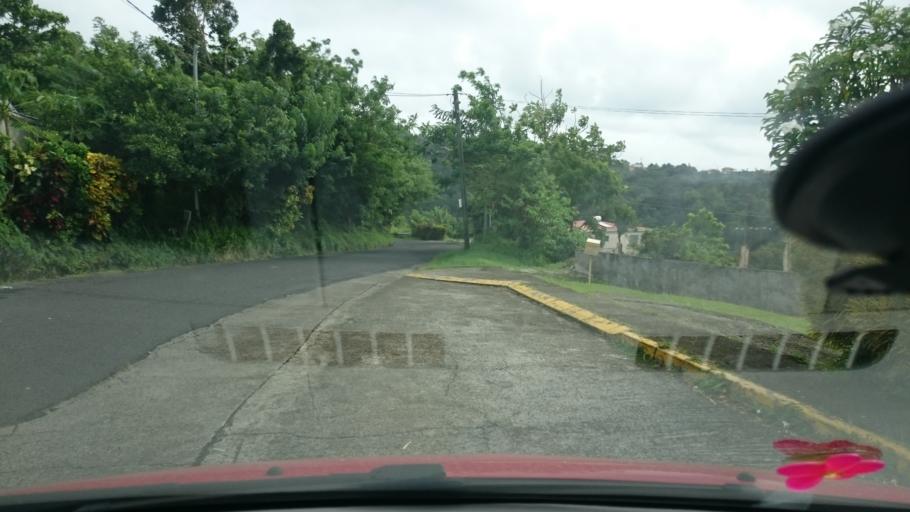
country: MQ
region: Martinique
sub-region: Martinique
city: Sainte-Luce
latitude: 14.4886
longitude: -60.9238
